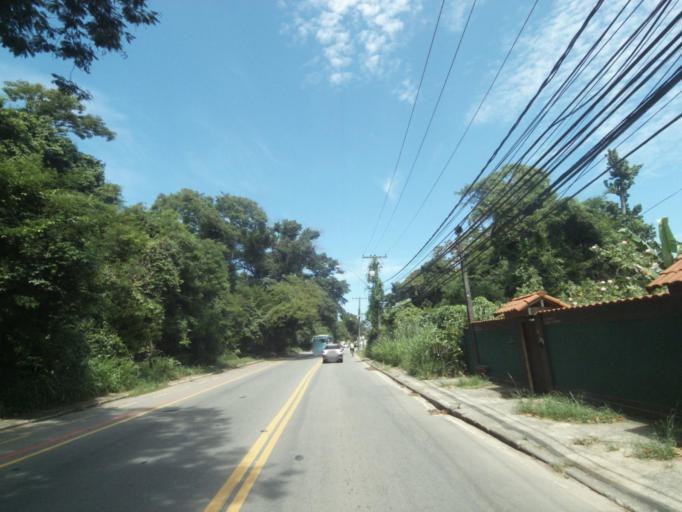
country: BR
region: Rio de Janeiro
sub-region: Niteroi
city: Niteroi
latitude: -22.9478
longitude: -43.0237
